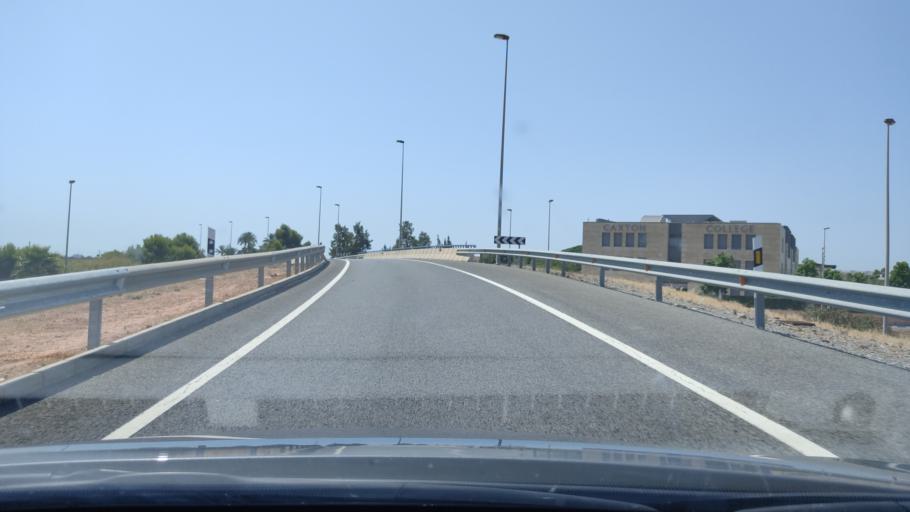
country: ES
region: Valencia
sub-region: Provincia de Valencia
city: Pucol
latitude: 39.6276
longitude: -0.3008
